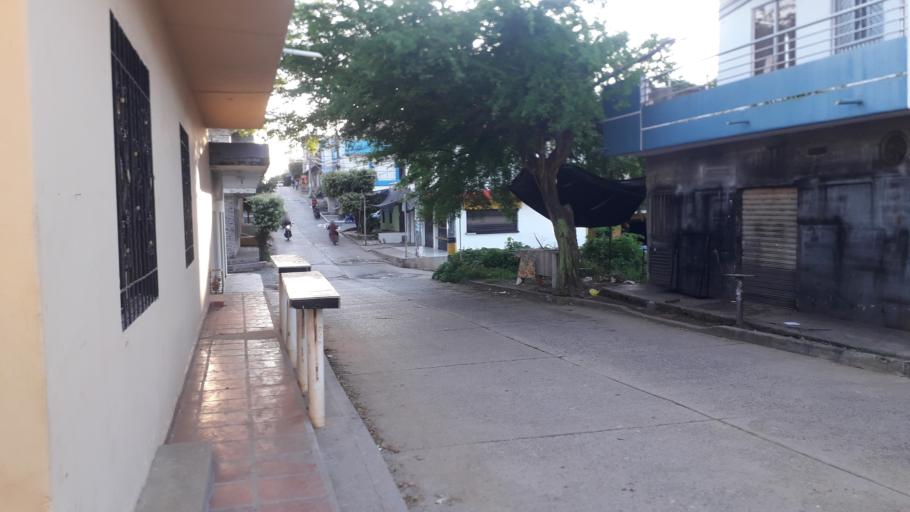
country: CO
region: Antioquia
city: Caucasia
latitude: 7.9774
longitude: -75.2049
